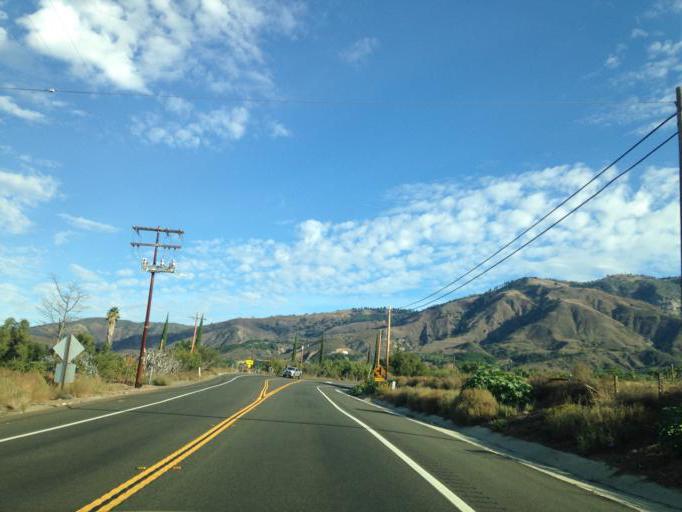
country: US
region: California
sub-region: San Diego County
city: Valley Center
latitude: 33.2967
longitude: -116.9435
